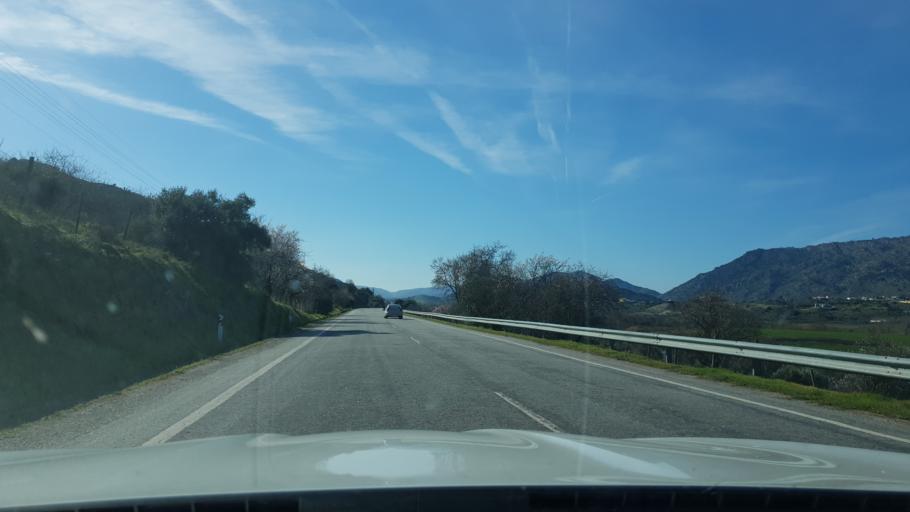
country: PT
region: Braganca
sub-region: Torre de Moncorvo
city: Torre de Moncorvo
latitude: 41.1956
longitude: -7.0967
